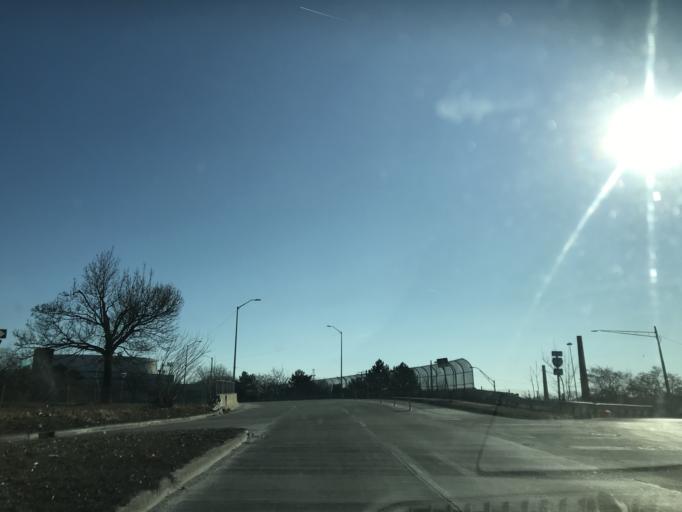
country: US
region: Michigan
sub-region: Wayne County
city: Grosse Pointe Park
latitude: 42.3963
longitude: -82.9896
